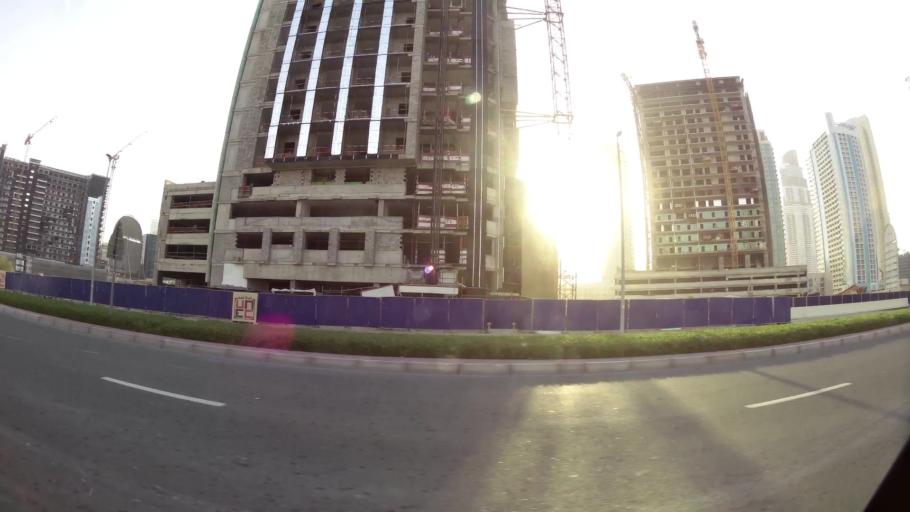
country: AE
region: Dubai
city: Dubai
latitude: 25.1887
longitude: 55.2839
